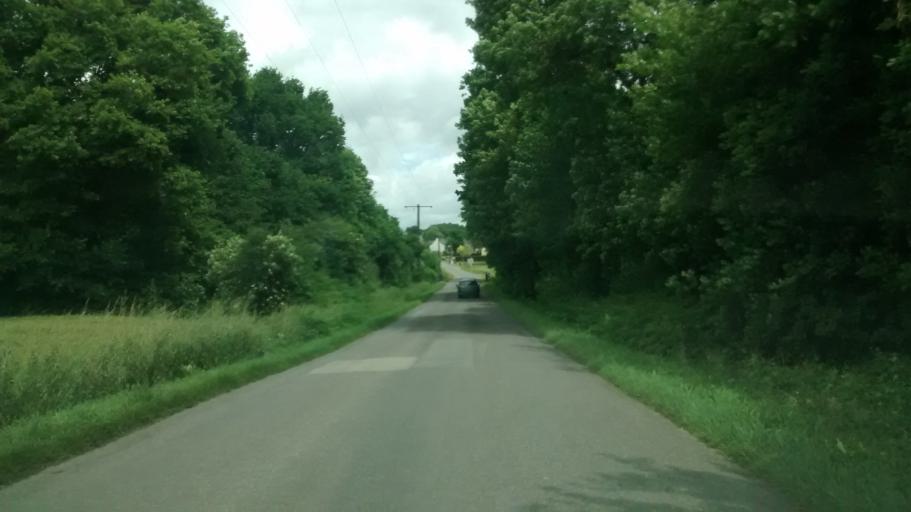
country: FR
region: Brittany
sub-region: Departement du Morbihan
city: La Gacilly
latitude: 47.7791
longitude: -2.1117
